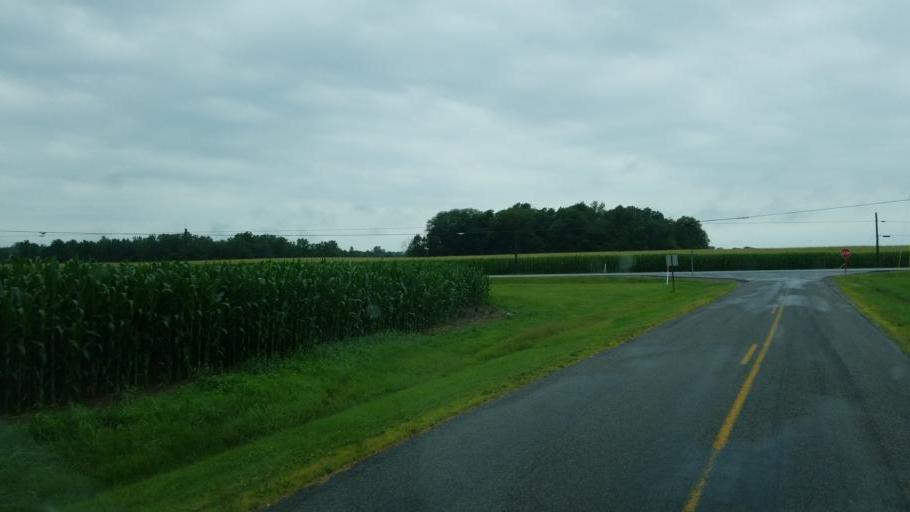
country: US
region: Ohio
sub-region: Hardin County
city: Kenton
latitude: 40.5084
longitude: -83.4995
